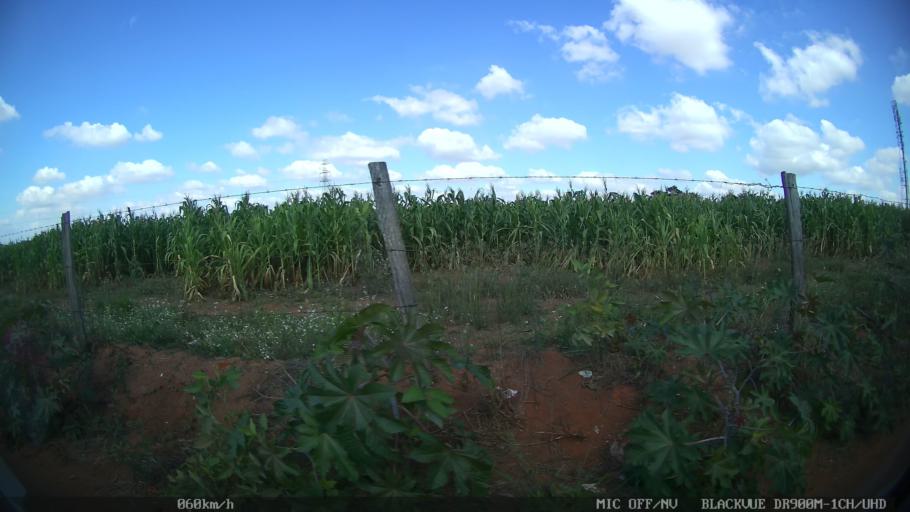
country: BR
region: Sao Paulo
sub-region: Hortolandia
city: Hortolandia
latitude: -22.8768
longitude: -47.2469
